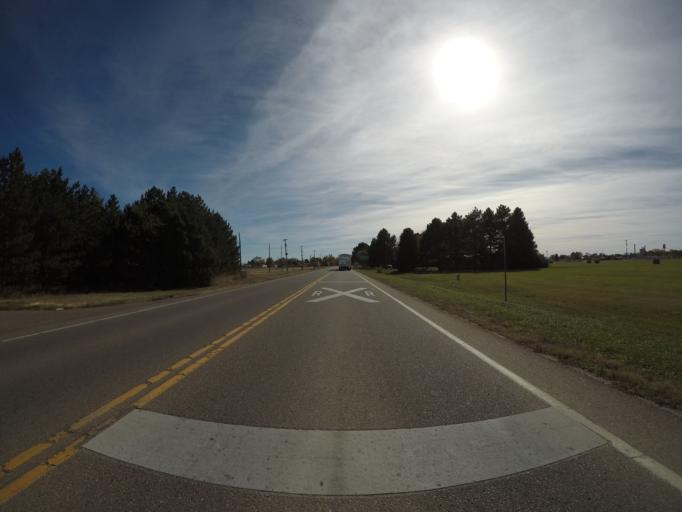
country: US
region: Colorado
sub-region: Kit Carson County
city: Burlington
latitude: 39.3111
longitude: -102.2601
